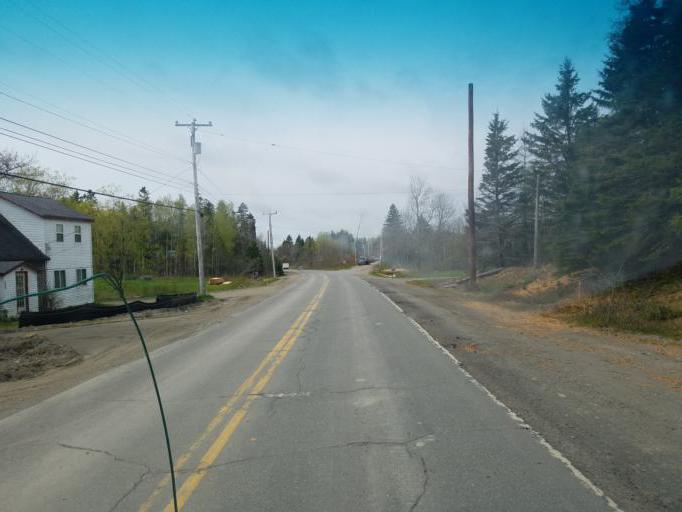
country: US
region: Maine
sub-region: Washington County
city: East Machias
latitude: 44.7865
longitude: -67.1866
